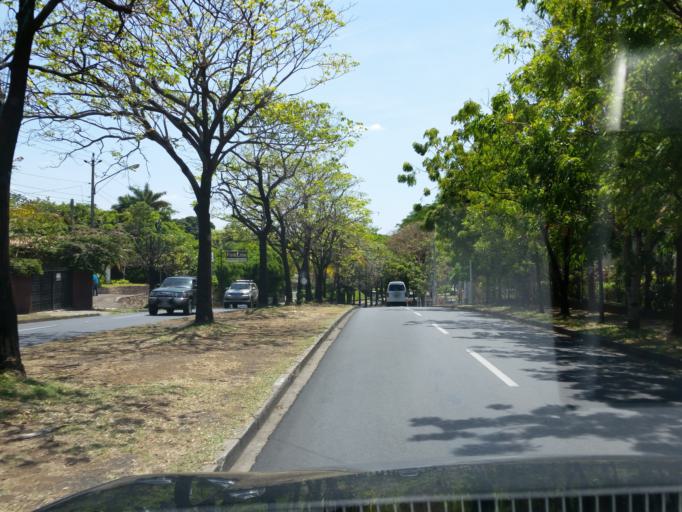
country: NI
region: Managua
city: Managua
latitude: 12.1028
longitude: -86.2668
